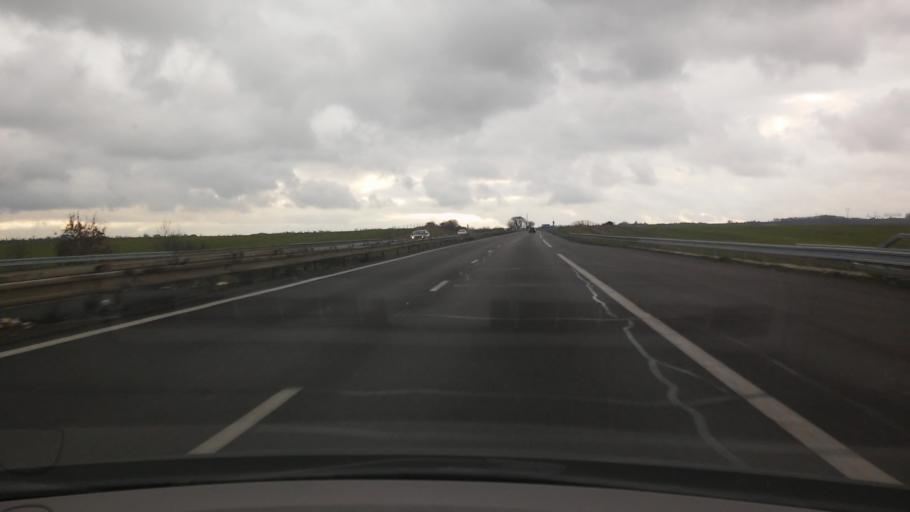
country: FR
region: Lorraine
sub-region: Departement de la Moselle
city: Argancy
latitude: 49.1722
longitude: 6.2503
